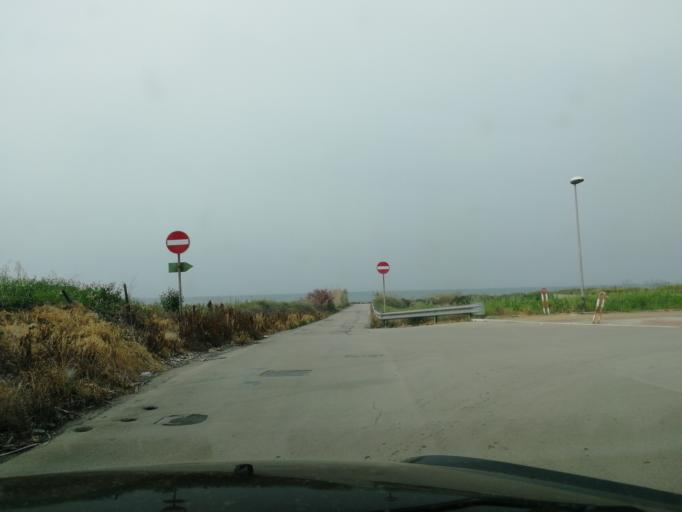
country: IT
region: Apulia
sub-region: Provincia di Barletta - Andria - Trani
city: Barletta
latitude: 41.3150
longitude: 16.3113
